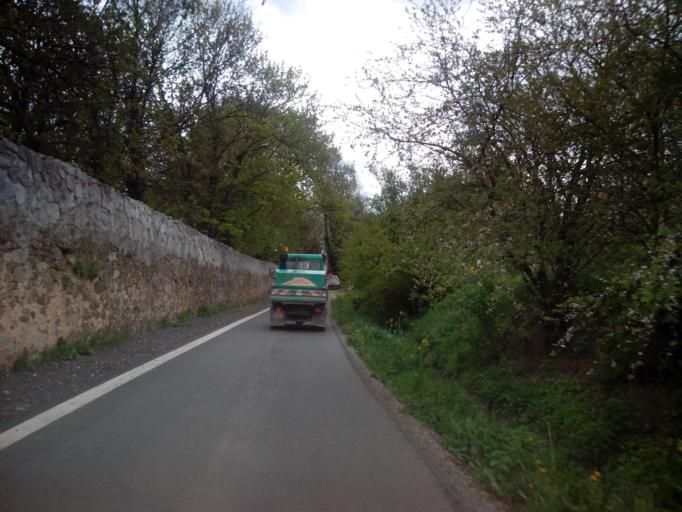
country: CZ
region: Central Bohemia
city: Revnice
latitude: 49.9068
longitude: 14.1486
